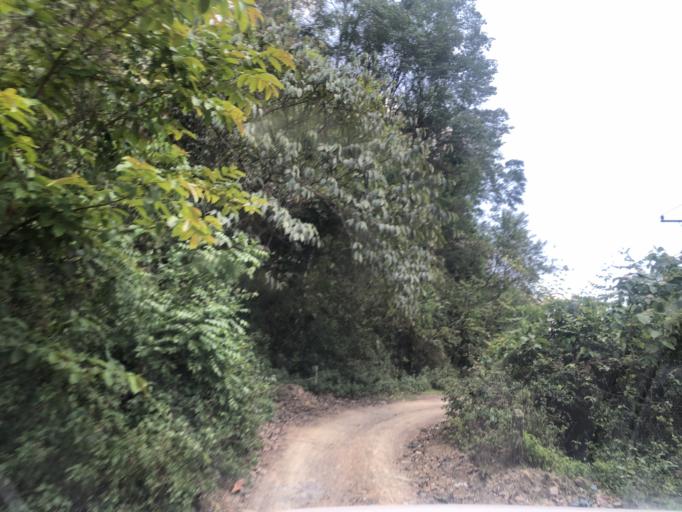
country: LA
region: Phongsali
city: Phongsali
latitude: 21.4489
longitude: 102.1628
